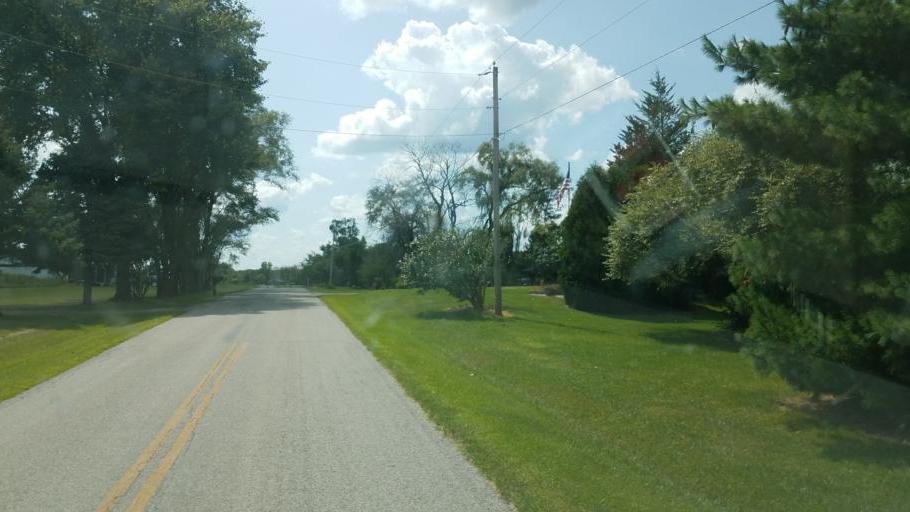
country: US
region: Ohio
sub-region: Delaware County
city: Sunbury
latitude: 40.3310
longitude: -82.8596
